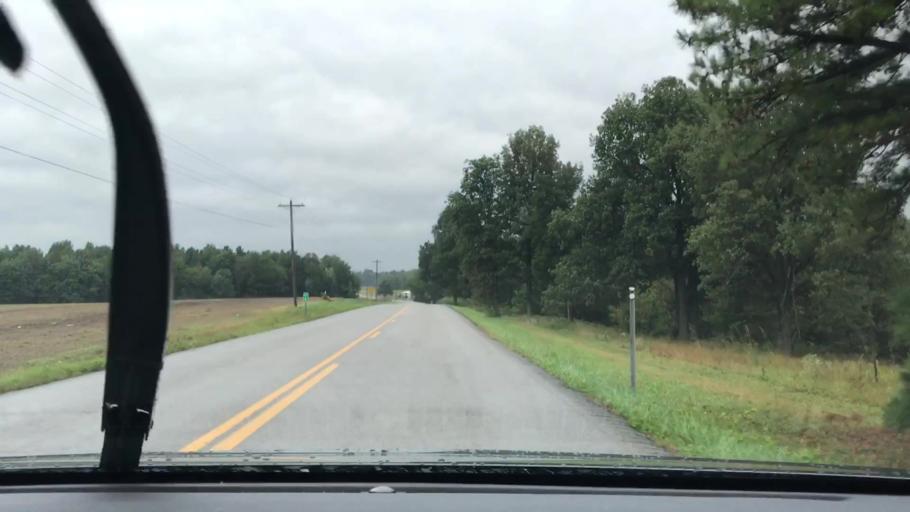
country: US
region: Kentucky
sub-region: McLean County
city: Calhoun
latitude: 37.4600
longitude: -87.2340
